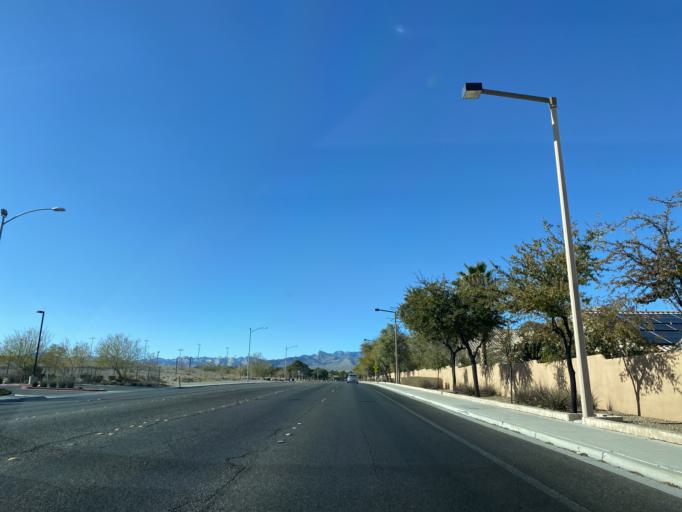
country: US
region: Nevada
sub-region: Clark County
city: Summerlin South
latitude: 36.1887
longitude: -115.2800
